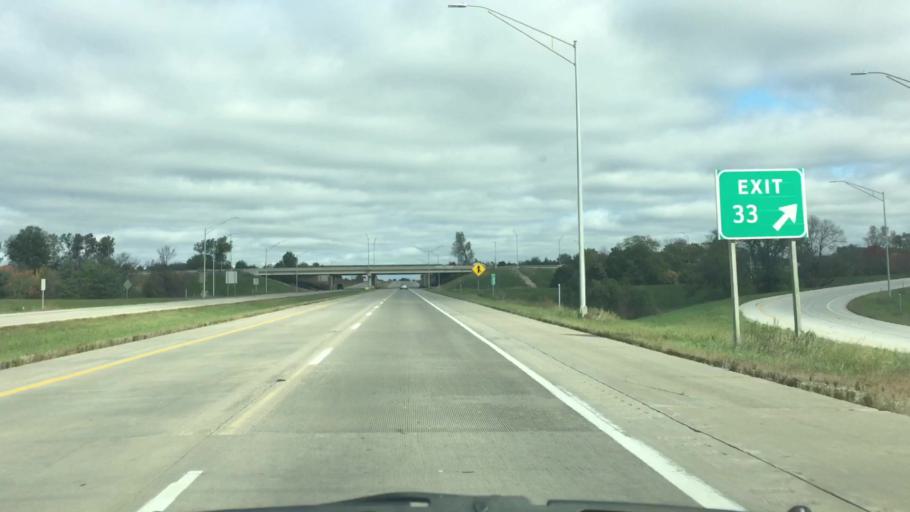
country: US
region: Iowa
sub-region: Clarke County
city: Osceola
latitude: 41.0239
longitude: -93.7941
